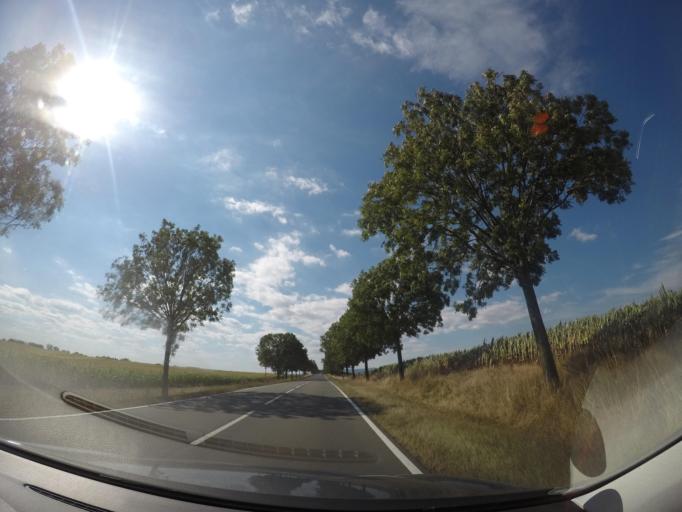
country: DE
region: Saxony-Anhalt
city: Langeln
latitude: 51.9348
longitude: 10.8110
